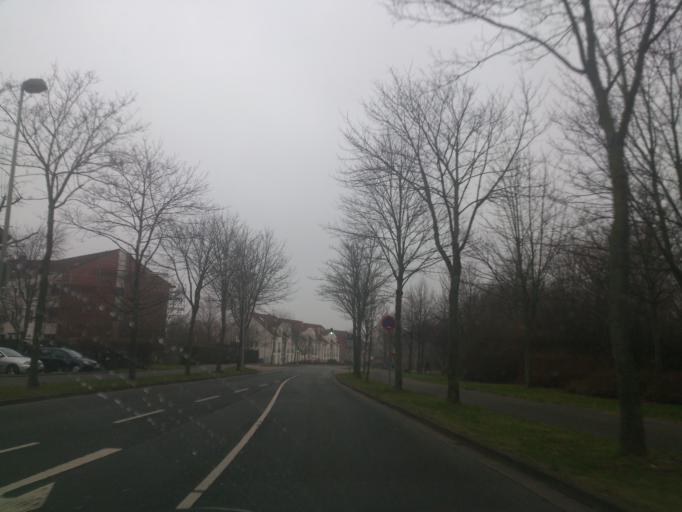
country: DE
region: North Rhine-Westphalia
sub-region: Regierungsbezirk Detmold
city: Paderborn
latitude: 51.7132
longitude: 8.7923
